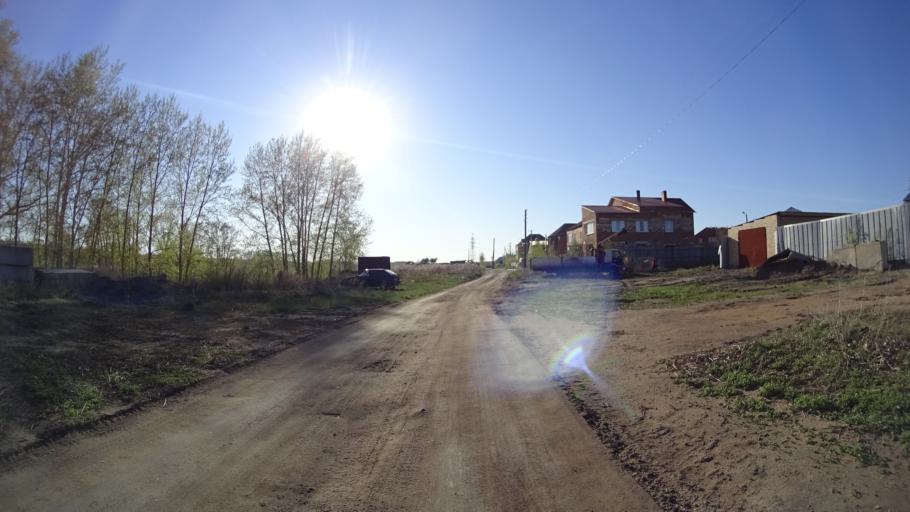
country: RU
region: Chelyabinsk
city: Troitsk
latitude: 54.0685
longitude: 61.5348
